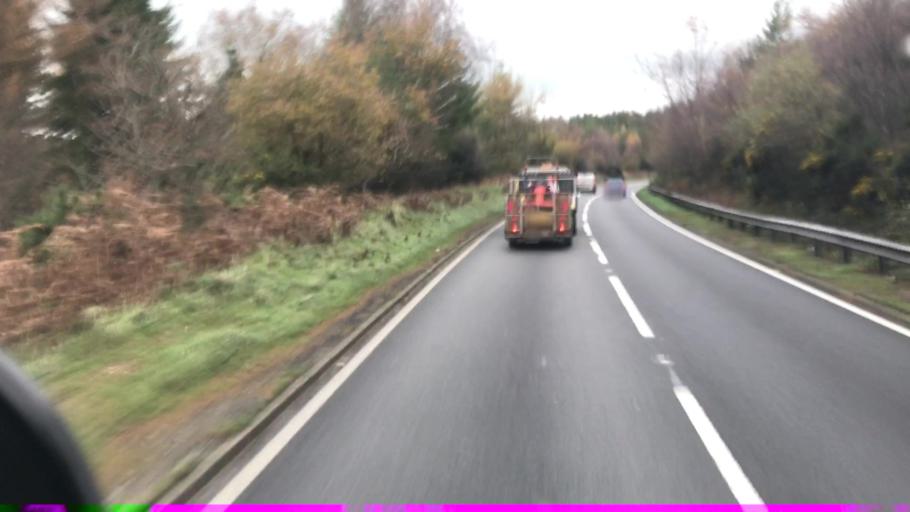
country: GB
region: England
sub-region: Devon
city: Chudleigh
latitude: 50.6343
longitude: -3.5658
